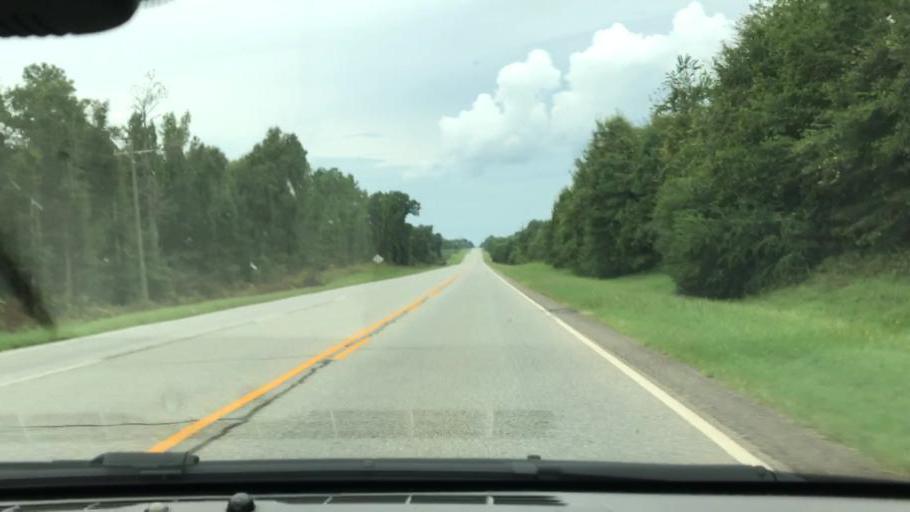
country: US
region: Georgia
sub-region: Early County
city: Blakely
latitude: 31.3092
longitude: -85.0465
